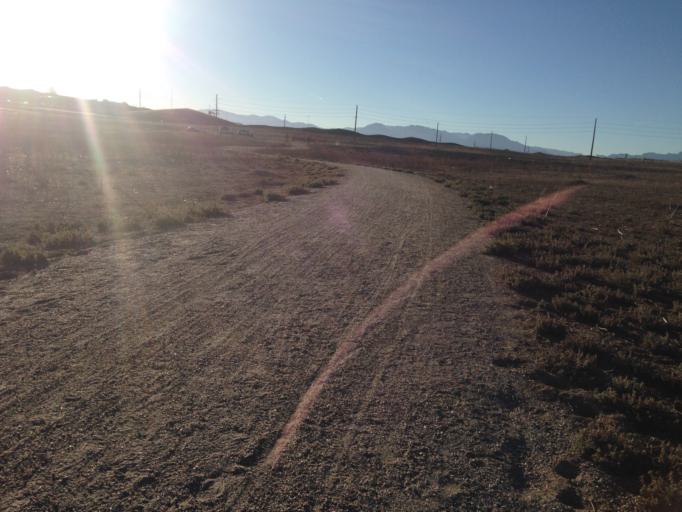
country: US
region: Colorado
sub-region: Broomfield County
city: Broomfield
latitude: 39.9358
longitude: -105.1165
